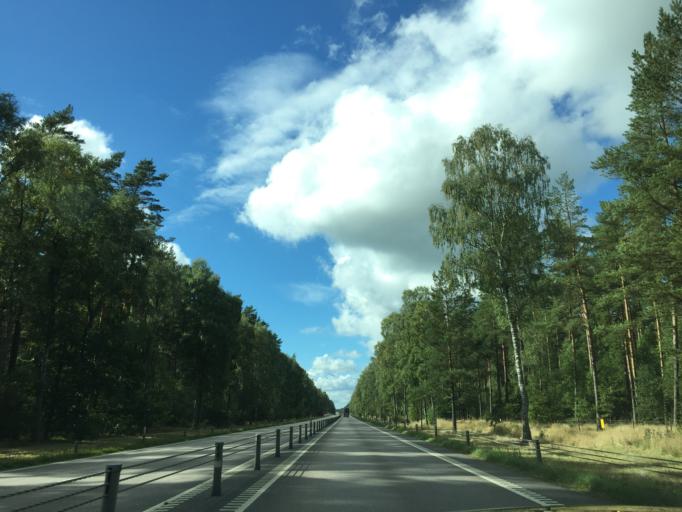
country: SE
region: Skane
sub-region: Sjobo Kommun
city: Sjoebo
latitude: 55.6383
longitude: 13.6432
